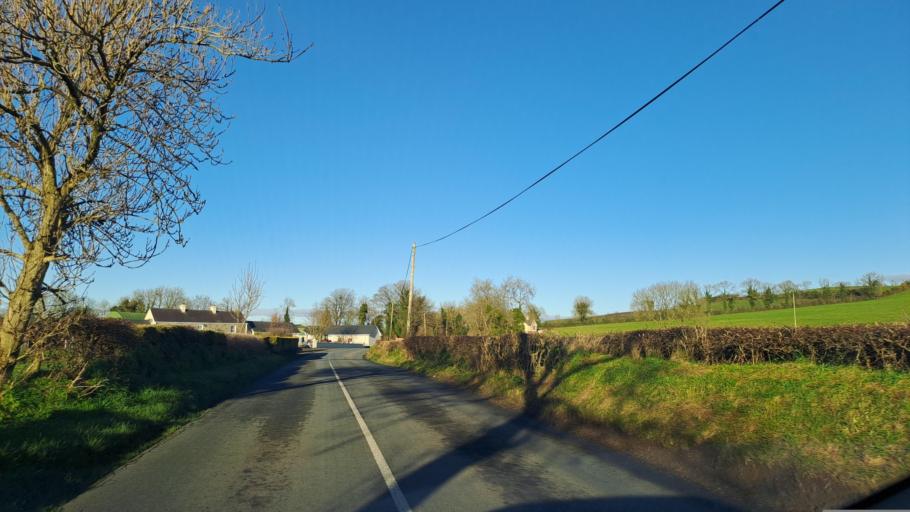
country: IE
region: Ulster
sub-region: An Cabhan
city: Mullagh
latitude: 53.8467
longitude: -6.9601
